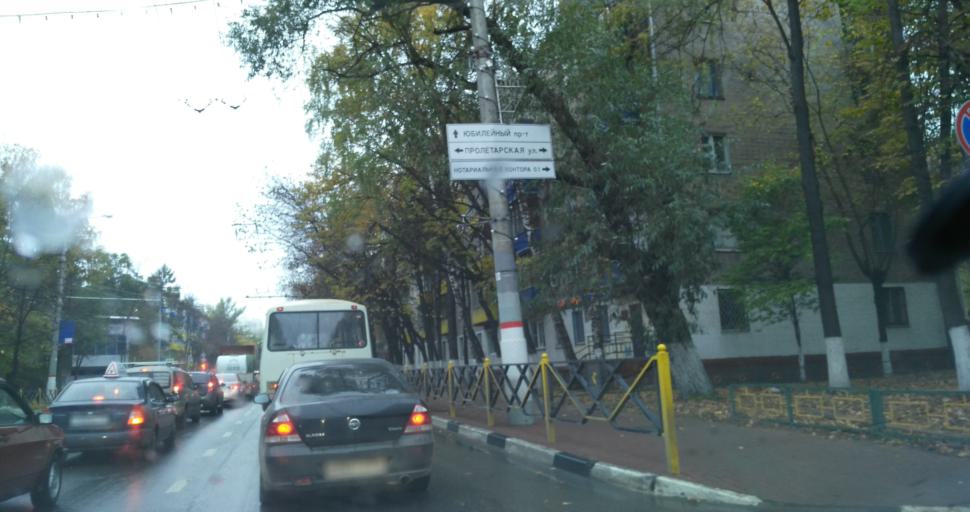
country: RU
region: Moscow
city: Khimki
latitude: 55.8931
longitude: 37.4415
